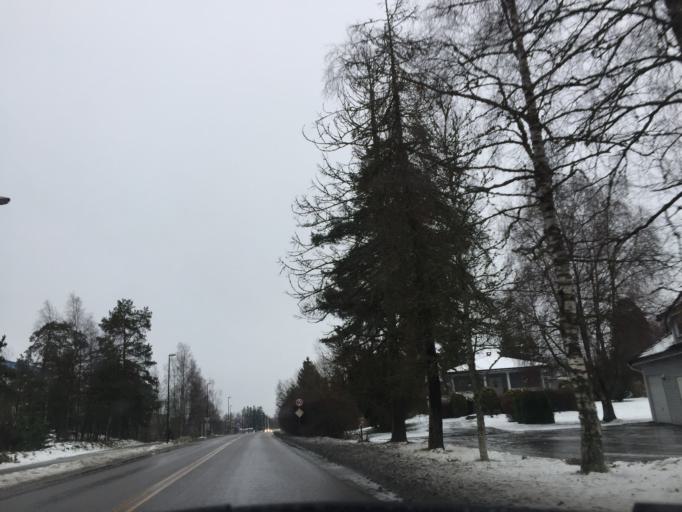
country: NO
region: Akershus
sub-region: Vestby
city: Vestby
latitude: 59.6228
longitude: 10.7397
